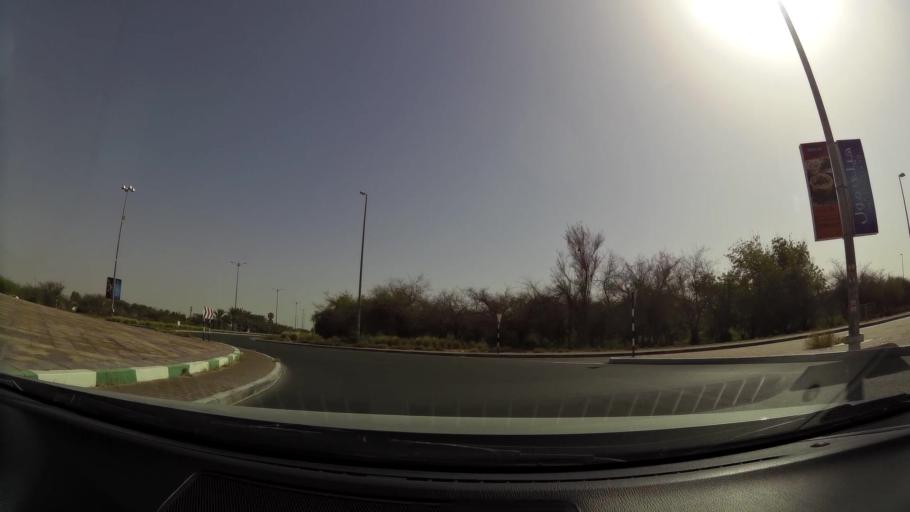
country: OM
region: Al Buraimi
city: Al Buraymi
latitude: 24.3392
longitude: 55.8059
